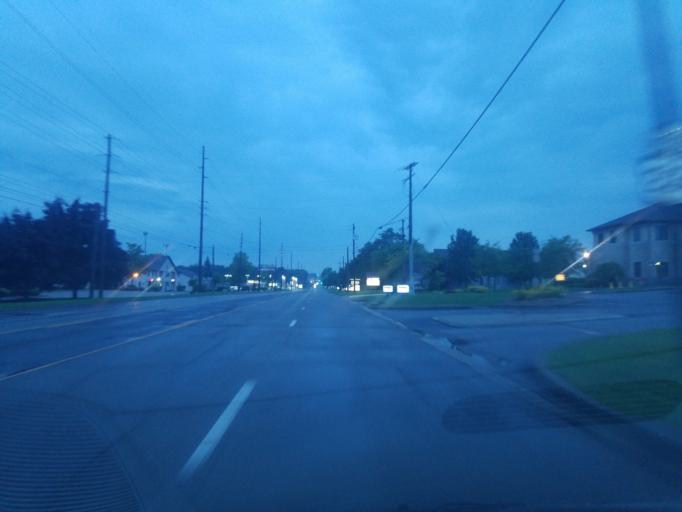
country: US
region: Ohio
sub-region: Mahoning County
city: Boardman
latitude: 41.0246
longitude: -80.6835
